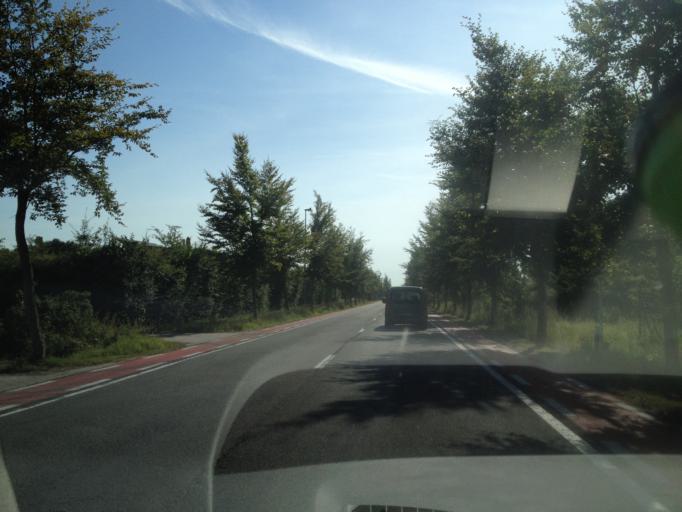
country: BE
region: Flanders
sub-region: Provincie West-Vlaanderen
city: Jabbeke
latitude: 51.1757
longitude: 3.0707
